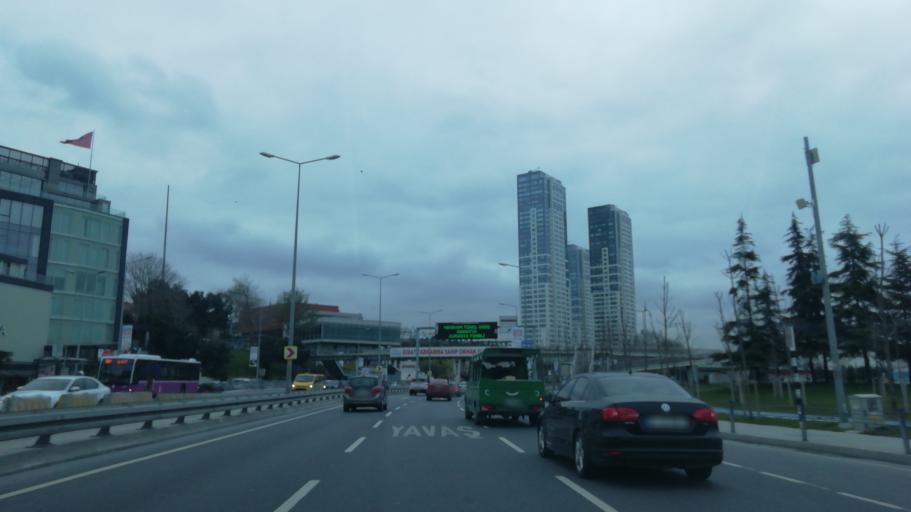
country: TR
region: Istanbul
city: Zeytinburnu
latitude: 40.9851
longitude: 28.9095
